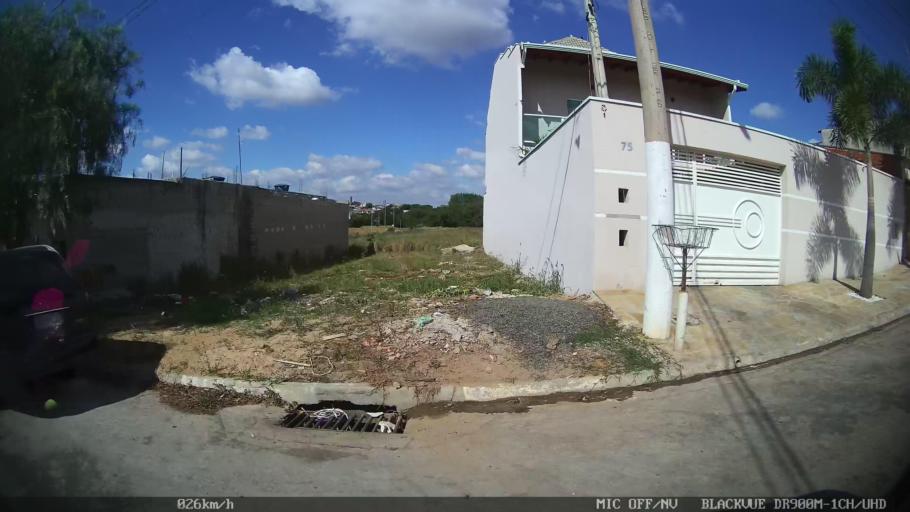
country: BR
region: Sao Paulo
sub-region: Hortolandia
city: Hortolandia
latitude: -22.8857
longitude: -47.2150
